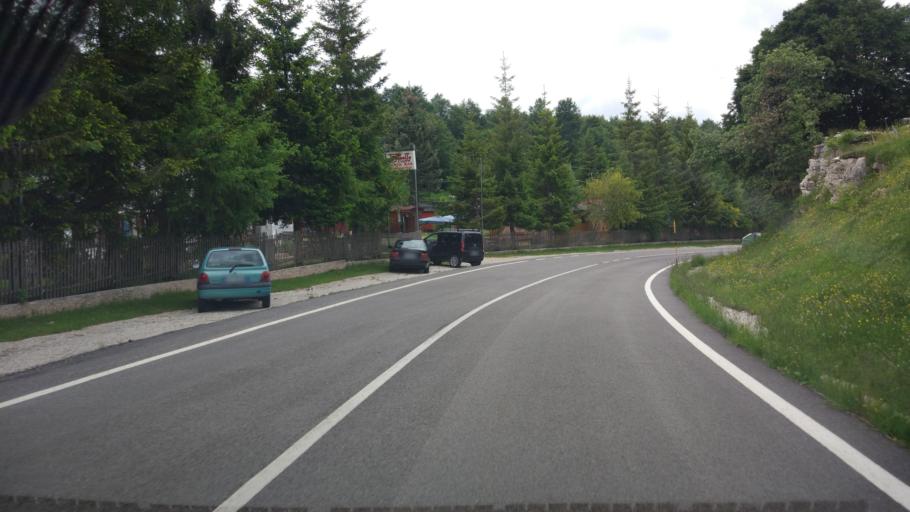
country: IT
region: Veneto
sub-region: Provincia di Verona
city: Bosco Chiesanuova
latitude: 45.6745
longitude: 11.0638
